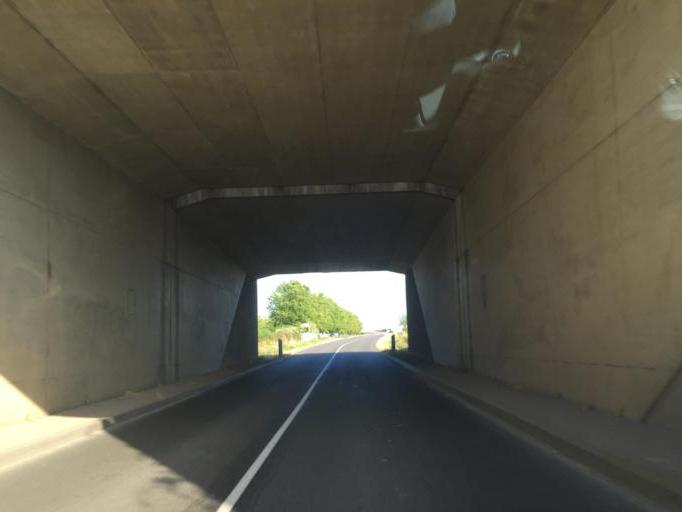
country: FR
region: Auvergne
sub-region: Departement de l'Allier
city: Toulon-sur-Allier
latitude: 46.5391
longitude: 3.3774
